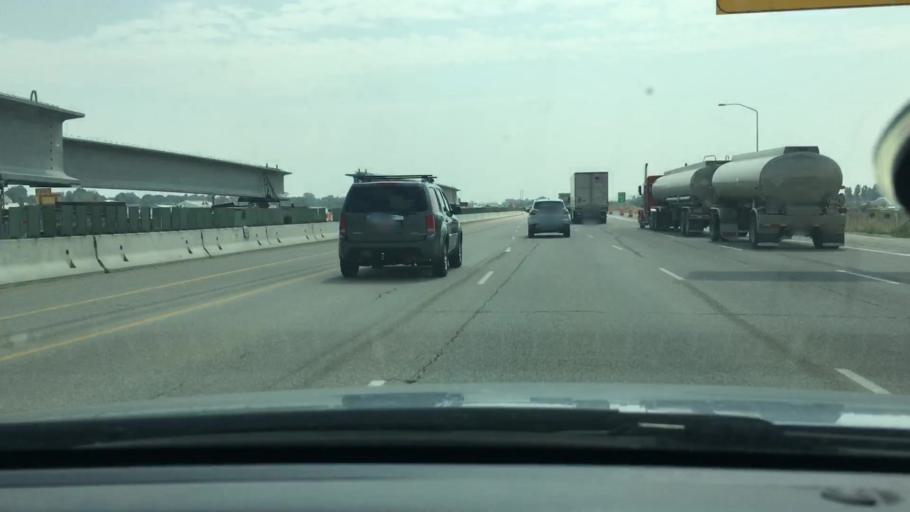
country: US
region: Utah
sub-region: Utah County
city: Lehi
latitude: 40.4181
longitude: -111.8759
